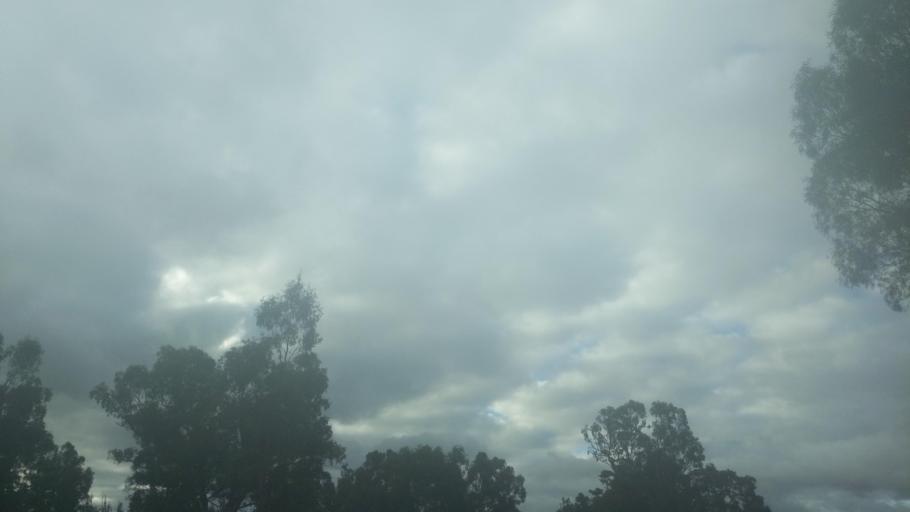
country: AU
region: New South Wales
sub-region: Wagga Wagga
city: Wagga Wagga
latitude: -35.0875
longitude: 147.3845
